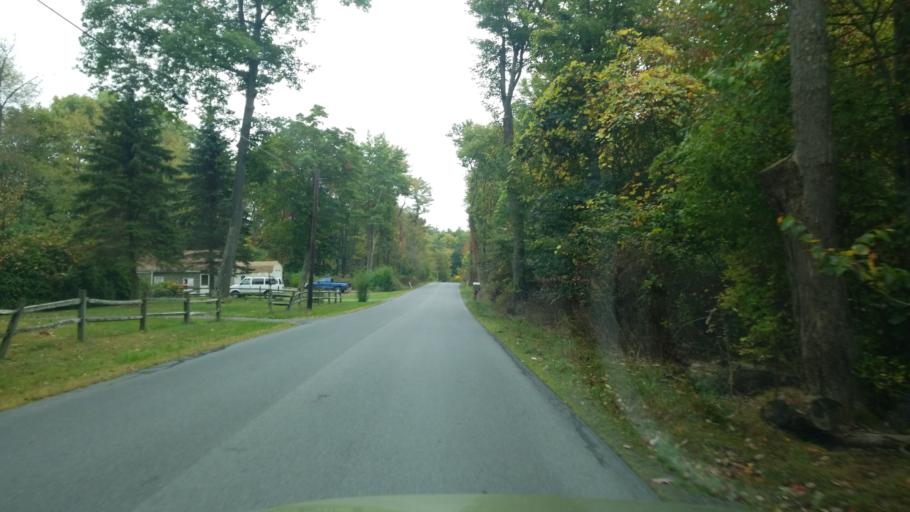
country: US
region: Pennsylvania
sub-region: Clearfield County
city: Curwensville
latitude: 41.0065
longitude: -78.5334
